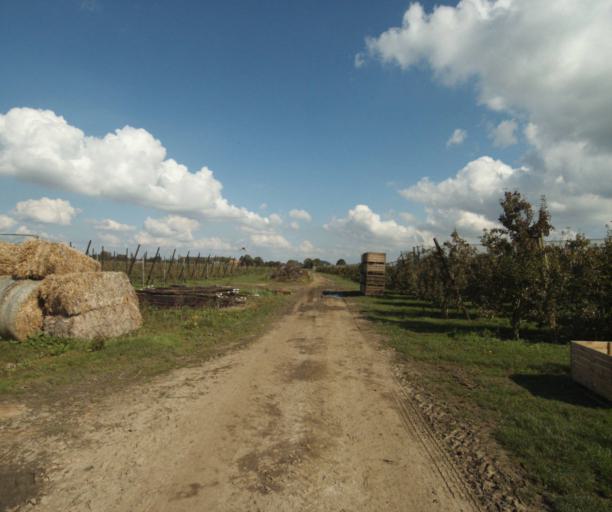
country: FR
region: Nord-Pas-de-Calais
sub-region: Departement du Nord
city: Aubers
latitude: 50.5829
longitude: 2.8294
